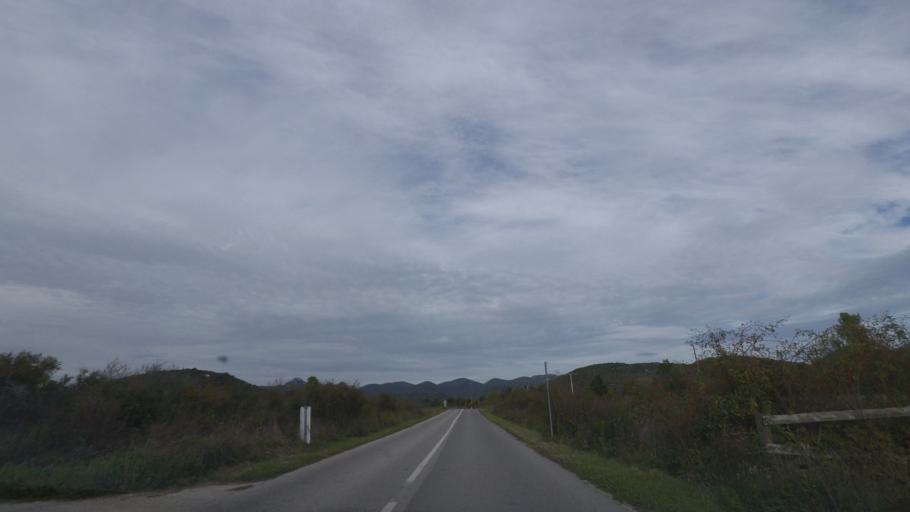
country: HR
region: Zadarska
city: Obrovac
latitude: 44.3745
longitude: 15.6689
